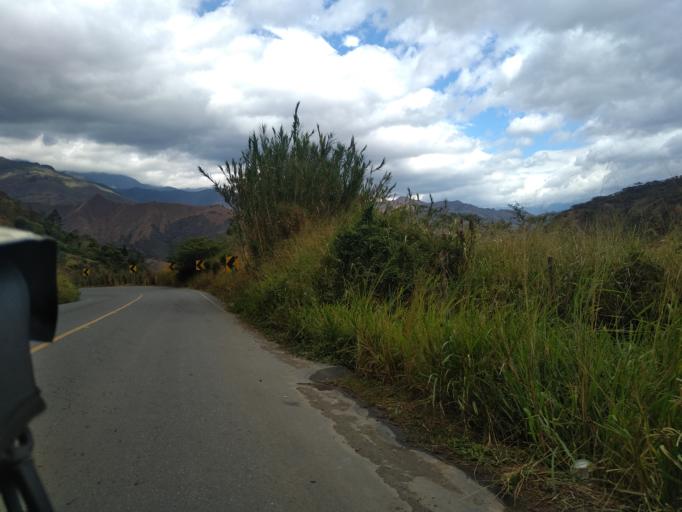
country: EC
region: Loja
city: Loja
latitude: -4.2325
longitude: -79.2307
